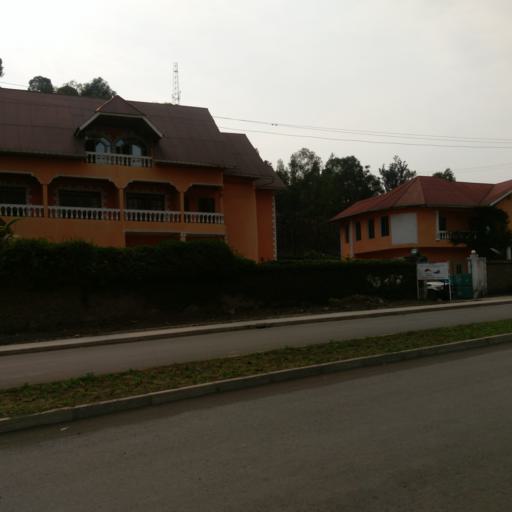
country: CD
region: Nord Kivu
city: Goma
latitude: -1.6841
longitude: 29.2287
